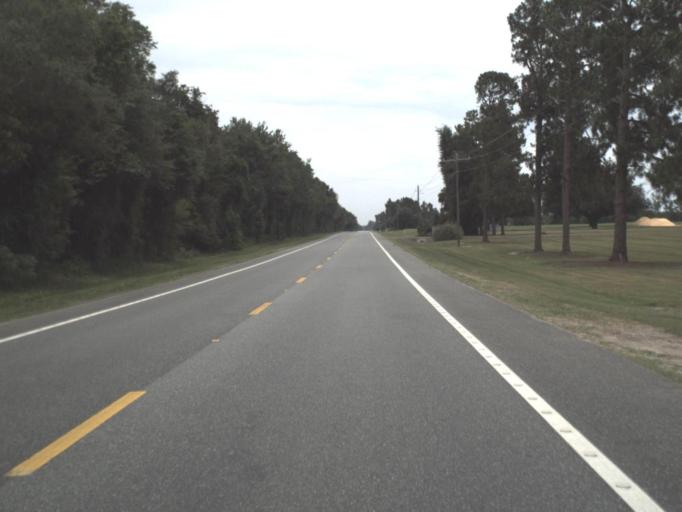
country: US
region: Florida
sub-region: Suwannee County
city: Wellborn
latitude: 30.1035
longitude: -82.9477
